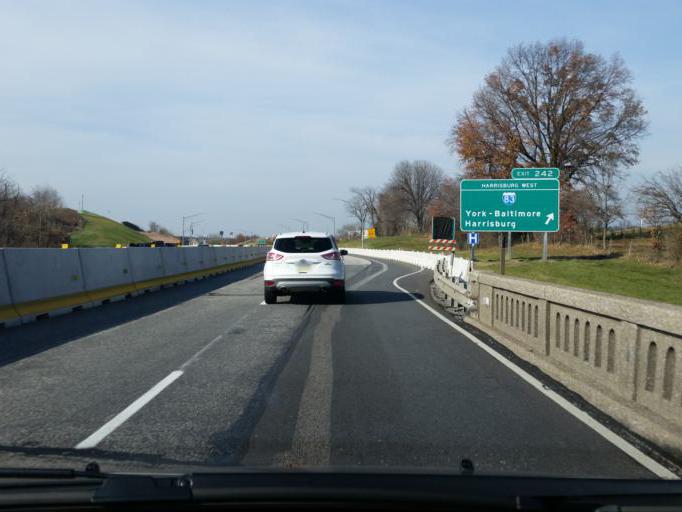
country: US
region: Pennsylvania
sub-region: Cumberland County
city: New Cumberland
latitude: 40.2109
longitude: -76.8687
